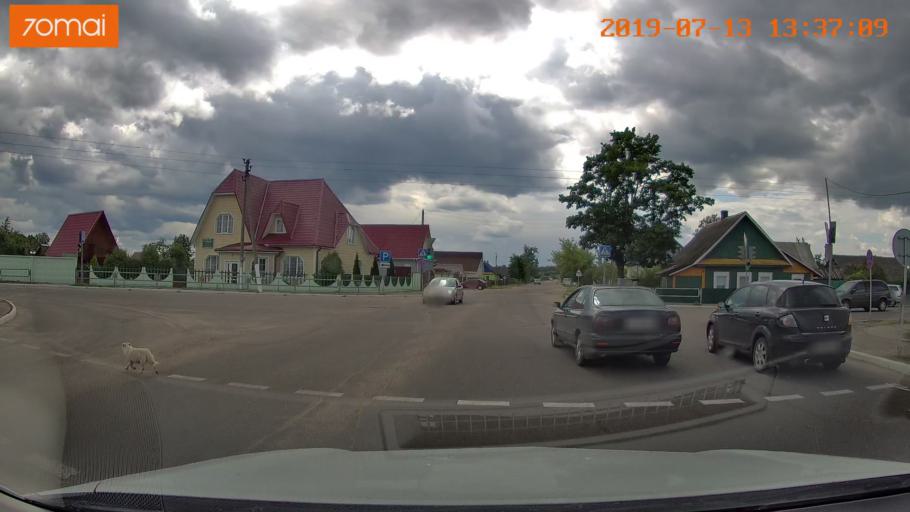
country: BY
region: Mogilev
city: Asipovichy
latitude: 53.3013
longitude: 28.6237
